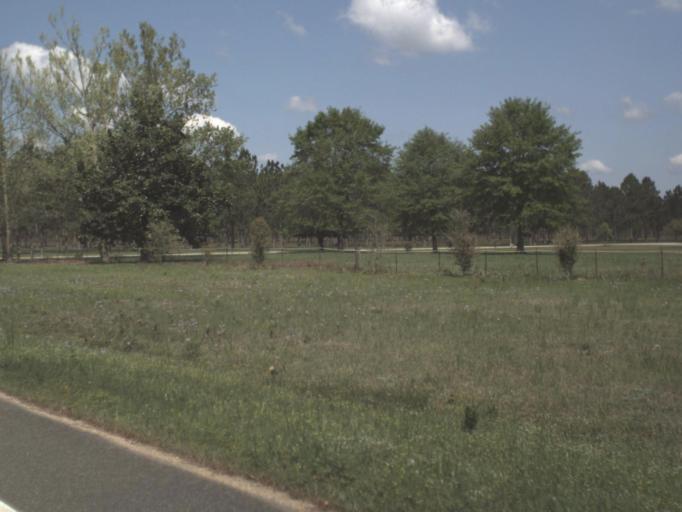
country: US
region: Florida
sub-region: Santa Rosa County
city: Point Baker
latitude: 30.8571
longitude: -86.8657
